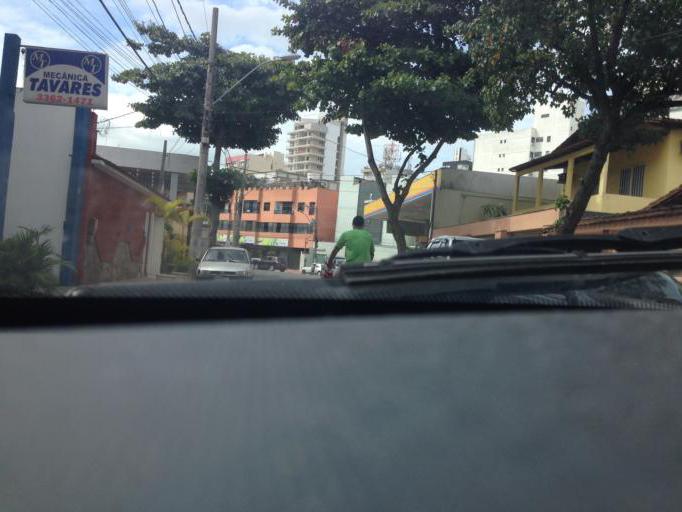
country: BR
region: Espirito Santo
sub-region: Guarapari
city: Guarapari
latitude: -20.6721
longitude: -40.5015
